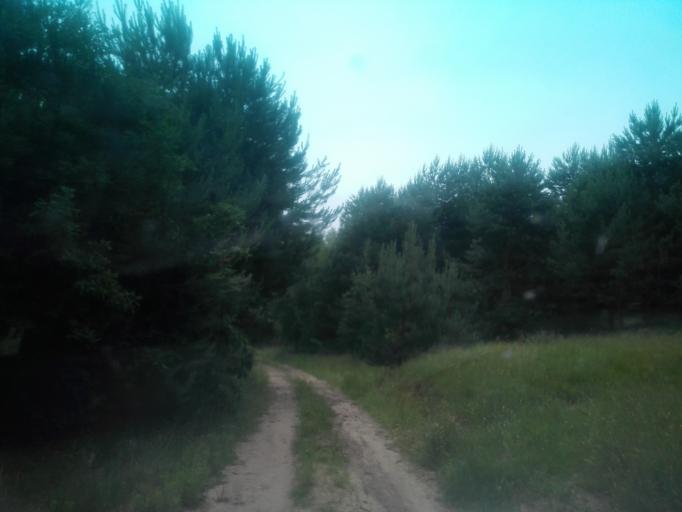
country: PL
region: Silesian Voivodeship
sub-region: Powiat czestochowski
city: Olsztyn
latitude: 50.7915
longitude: 19.2543
